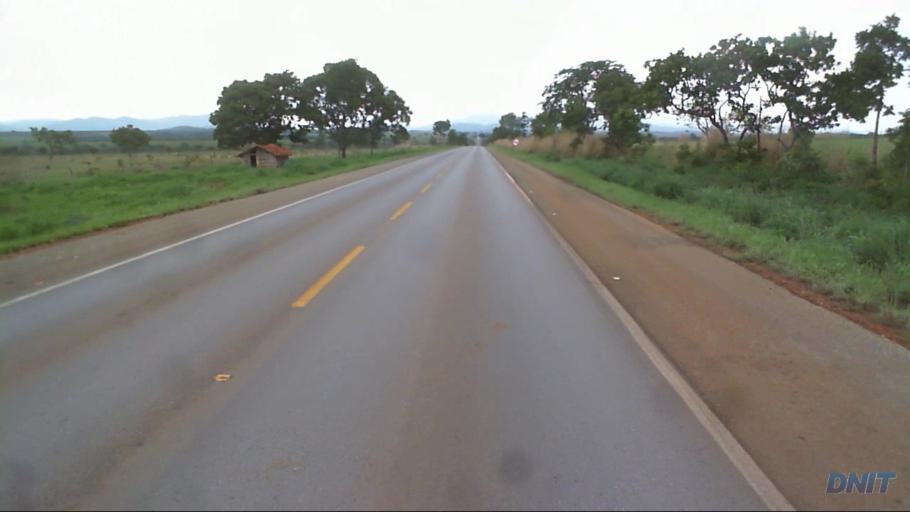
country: BR
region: Goias
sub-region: Barro Alto
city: Barro Alto
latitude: -14.7981
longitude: -49.0499
